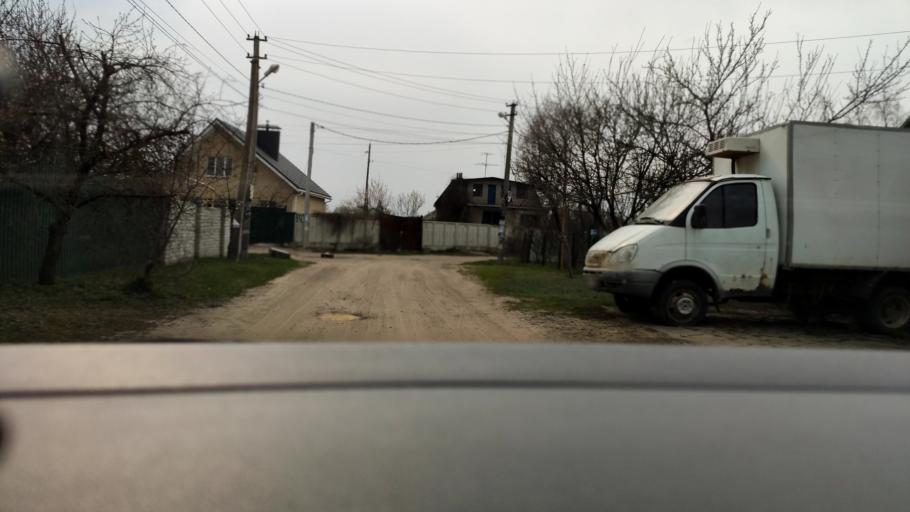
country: RU
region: Voronezj
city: Pridonskoy
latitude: 51.6597
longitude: 39.0903
